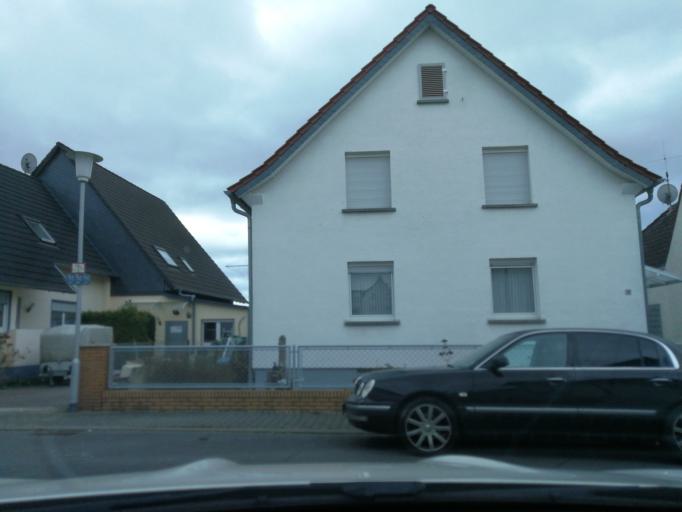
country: DE
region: Hesse
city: Reinheim
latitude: 49.8465
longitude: 8.8033
